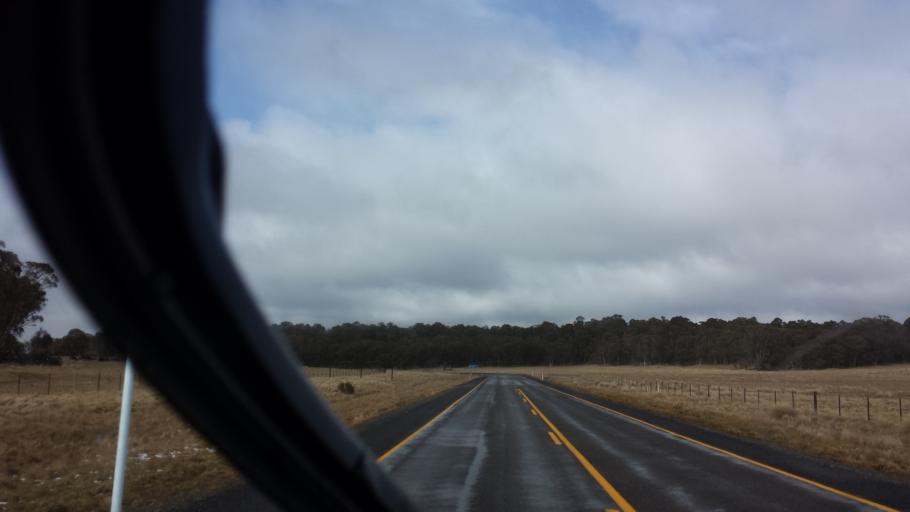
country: AU
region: Victoria
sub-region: Alpine
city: Mount Beauty
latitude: -37.0541
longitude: 147.3248
